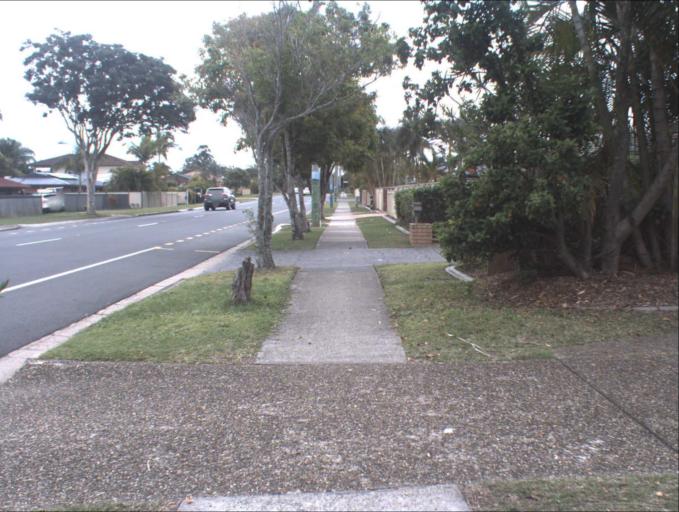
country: AU
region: Queensland
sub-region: Brisbane
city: Sunnybank Hills
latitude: -27.6618
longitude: 153.0228
